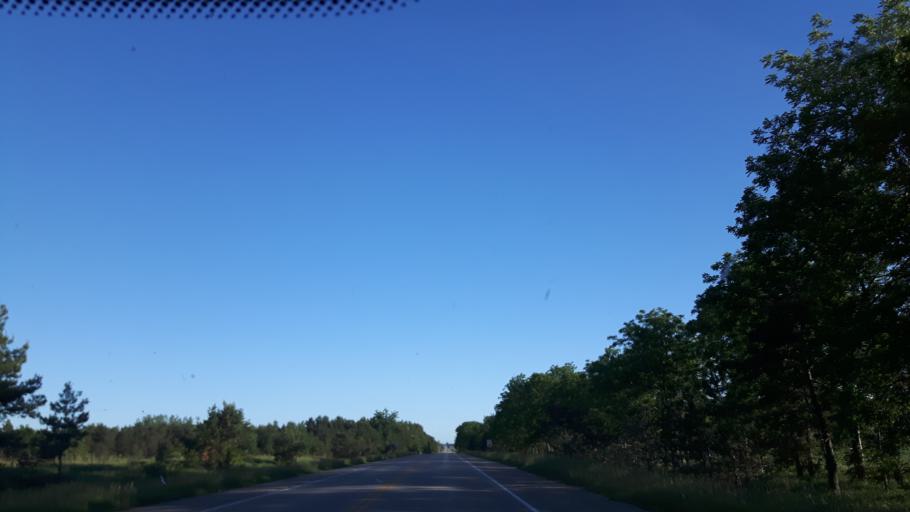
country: CA
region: Ontario
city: Goderich
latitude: 43.6404
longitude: -81.6025
